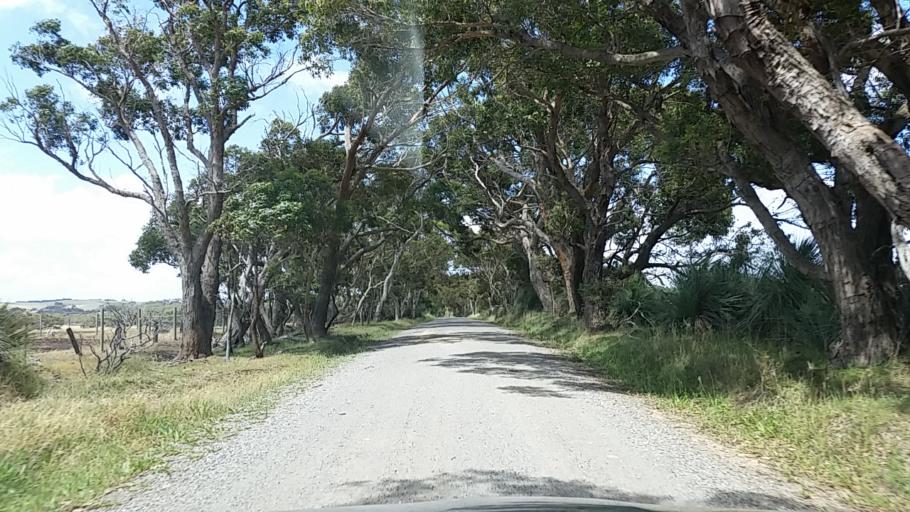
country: AU
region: South Australia
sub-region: Alexandrina
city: Mount Compass
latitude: -35.4371
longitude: 138.5856
